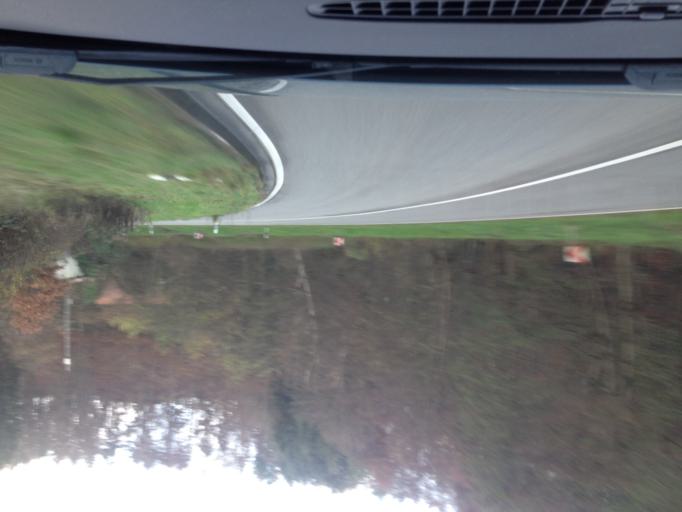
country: DE
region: Rheinland-Pfalz
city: Weidenthal
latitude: 49.3997
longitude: 8.0200
